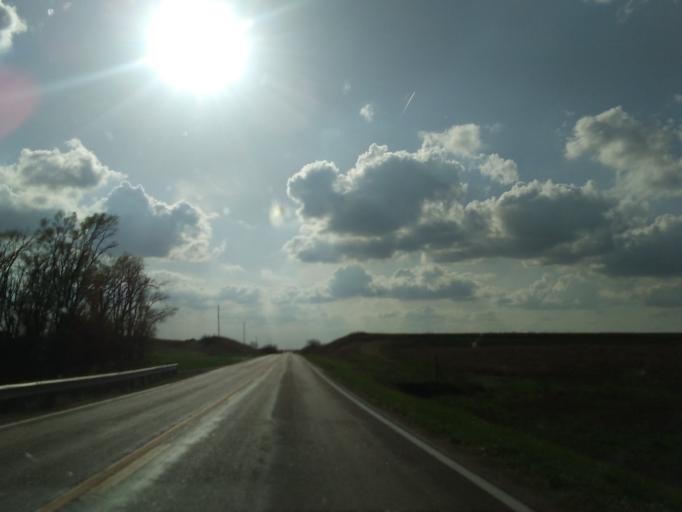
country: US
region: Nebraska
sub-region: Webster County
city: Red Cloud
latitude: 40.0890
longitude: -98.5859
